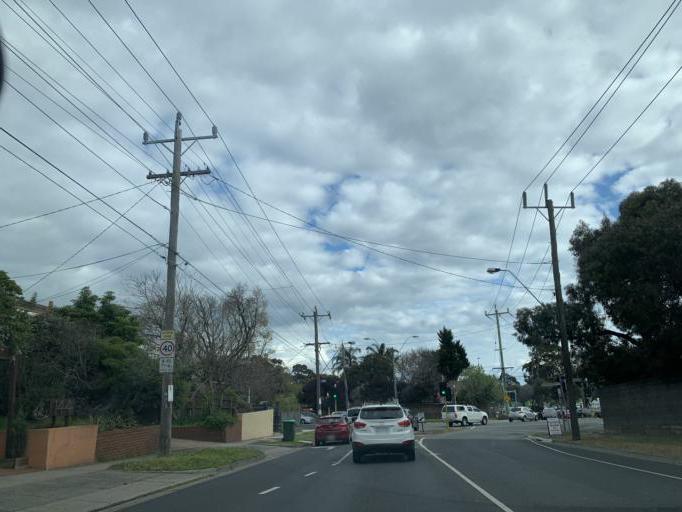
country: AU
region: Victoria
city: Beaumaris
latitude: -37.9772
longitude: 145.0348
